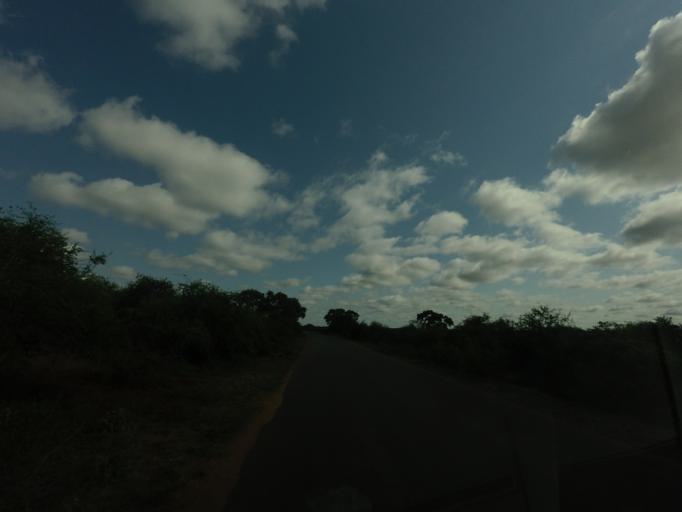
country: ZA
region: Mpumalanga
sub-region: Ehlanzeni District
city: Komatipoort
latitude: -25.1338
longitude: 31.9437
